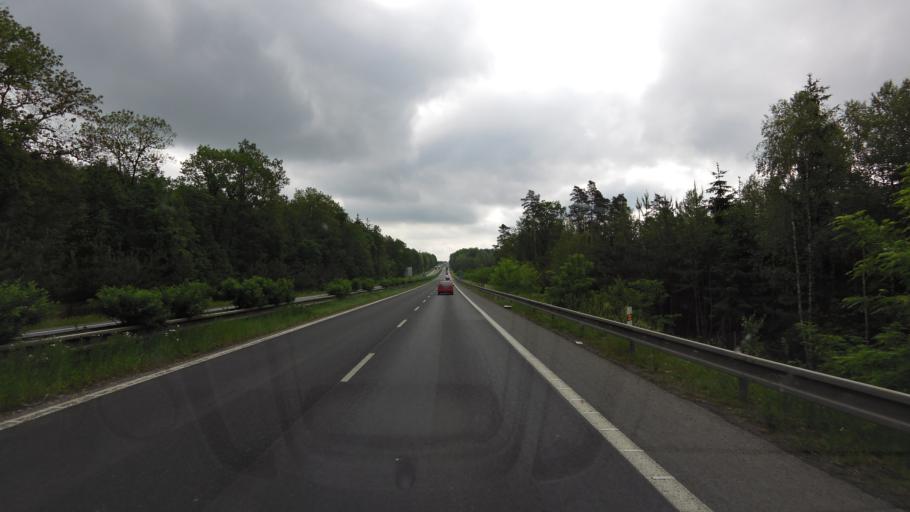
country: CZ
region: Plzensky
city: Dysina
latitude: 49.7463
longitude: 13.4566
